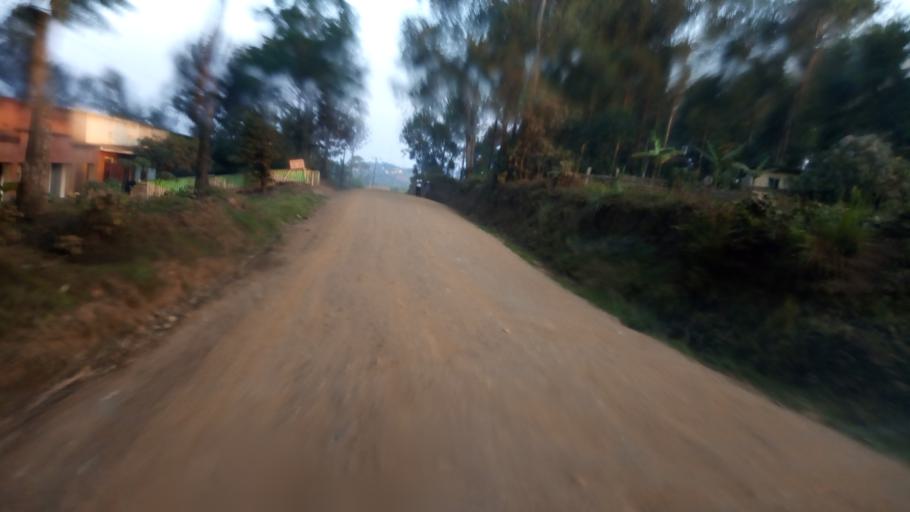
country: UG
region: Western Region
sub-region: Rukungiri District
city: Rukungiri
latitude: -0.7722
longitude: 29.9264
